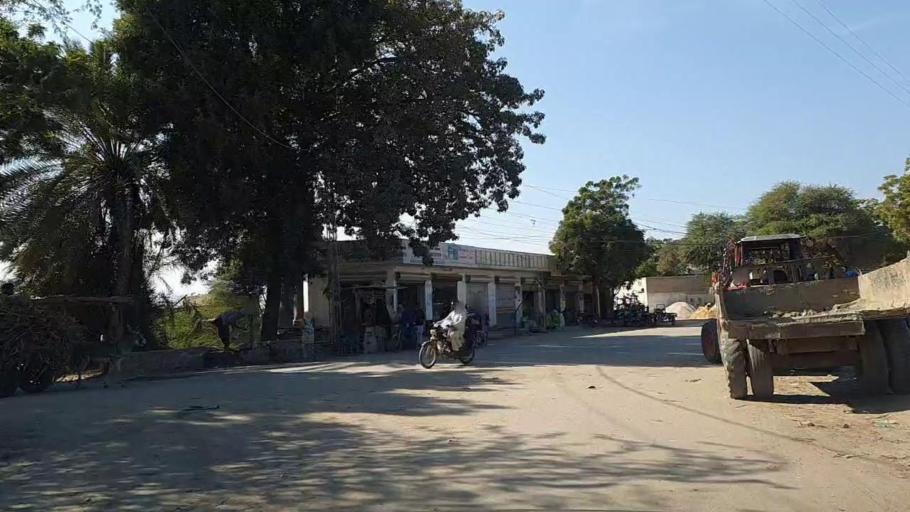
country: PK
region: Sindh
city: Nawabshah
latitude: 26.2284
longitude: 68.4173
